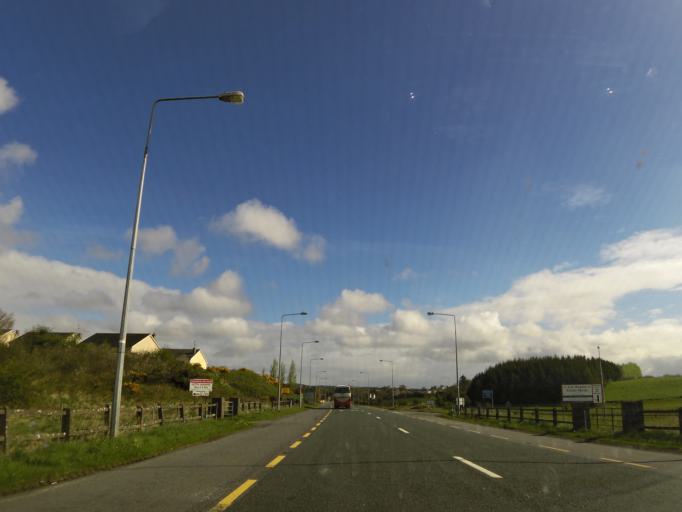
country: IE
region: Connaught
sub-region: Maigh Eo
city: Swinford
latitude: 53.8662
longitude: -8.8524
